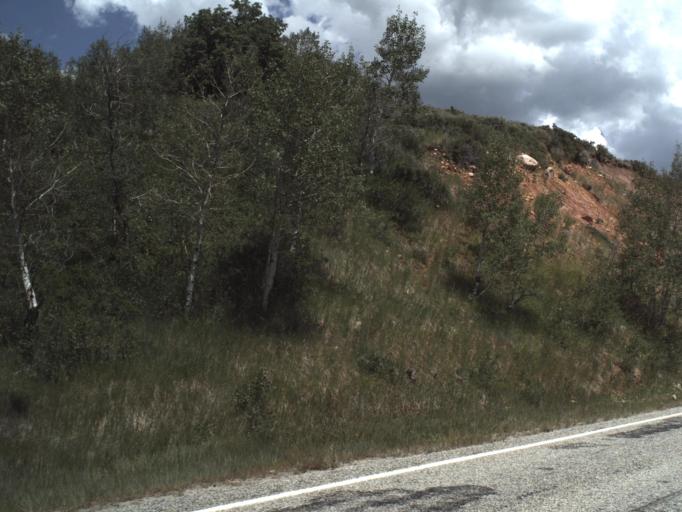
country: US
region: Utah
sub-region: Weber County
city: Wolf Creek
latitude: 41.4172
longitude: -111.5780
